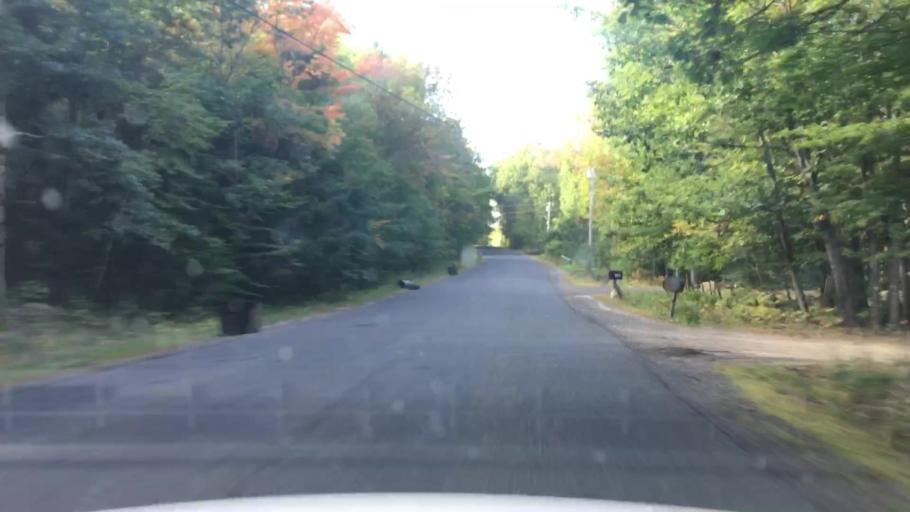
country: US
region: Maine
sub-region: Androscoggin County
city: Lisbon Falls
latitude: 43.9587
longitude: -70.0514
